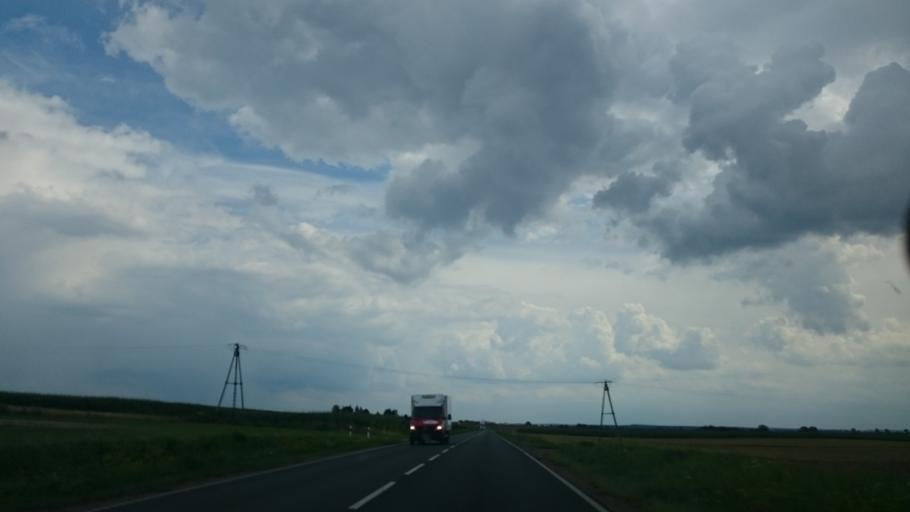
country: PL
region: Pomeranian Voivodeship
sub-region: Powiat chojnicki
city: Chojnice
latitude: 53.6662
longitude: 17.6655
